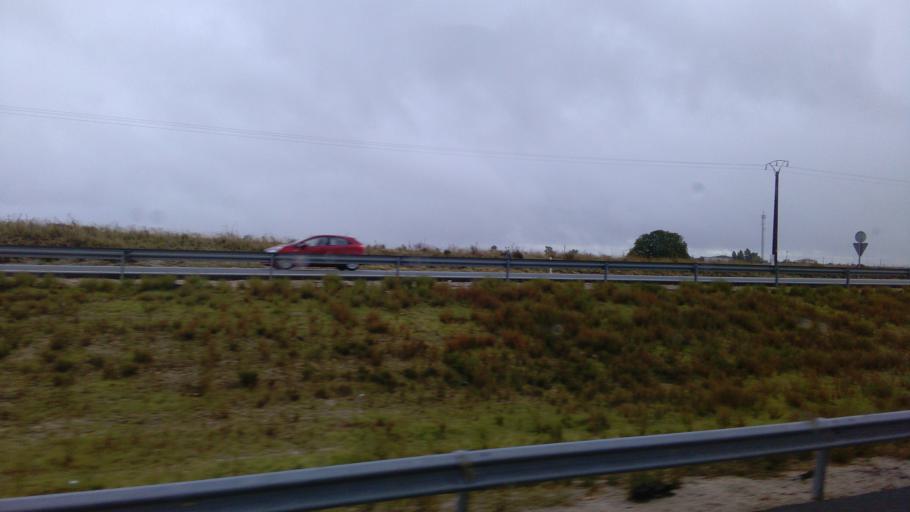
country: ES
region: Castille-La Mancha
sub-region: Province of Toledo
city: La Torre de Esteban Hambran
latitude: 40.1614
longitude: -4.1705
